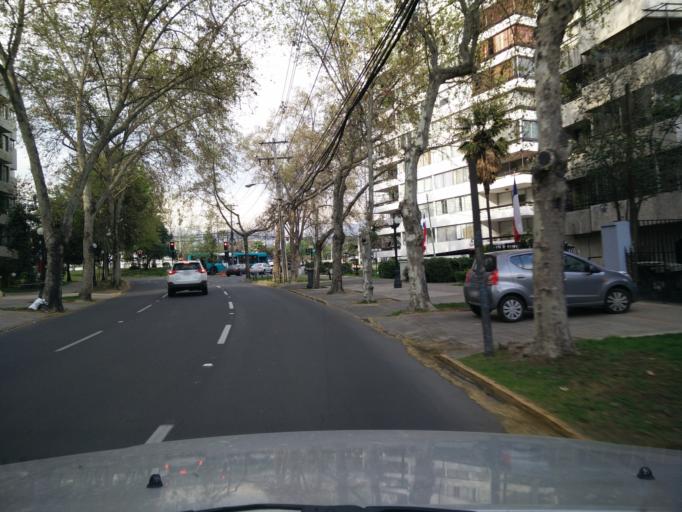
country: CL
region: Santiago Metropolitan
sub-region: Provincia de Santiago
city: Villa Presidente Frei, Nunoa, Santiago, Chile
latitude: -33.4249
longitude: -70.5940
